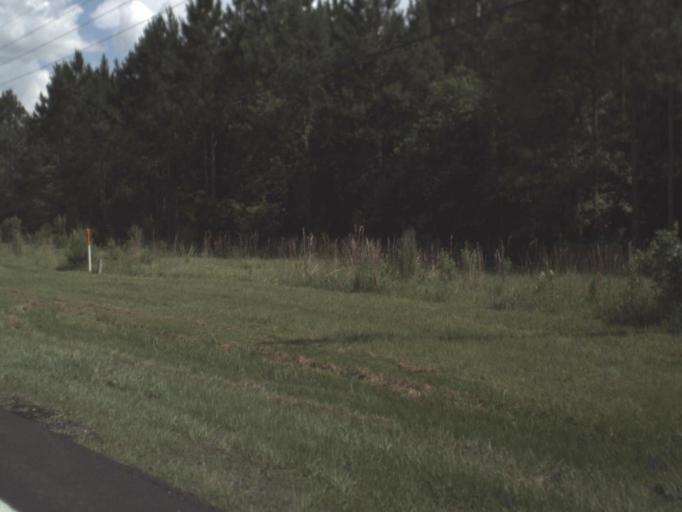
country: US
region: Florida
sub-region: Alachua County
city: Alachua
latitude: 29.7624
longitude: -82.4054
